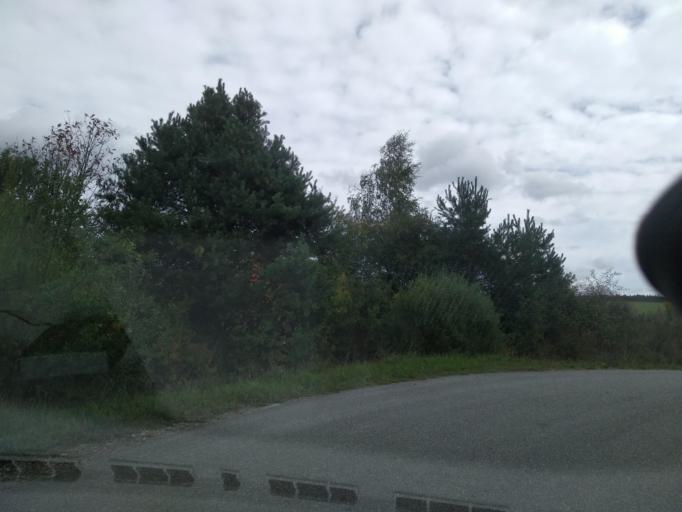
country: PL
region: Lesser Poland Voivodeship
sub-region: Powiat gorlicki
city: Uscie Gorlickie
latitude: 49.5184
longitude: 21.1487
